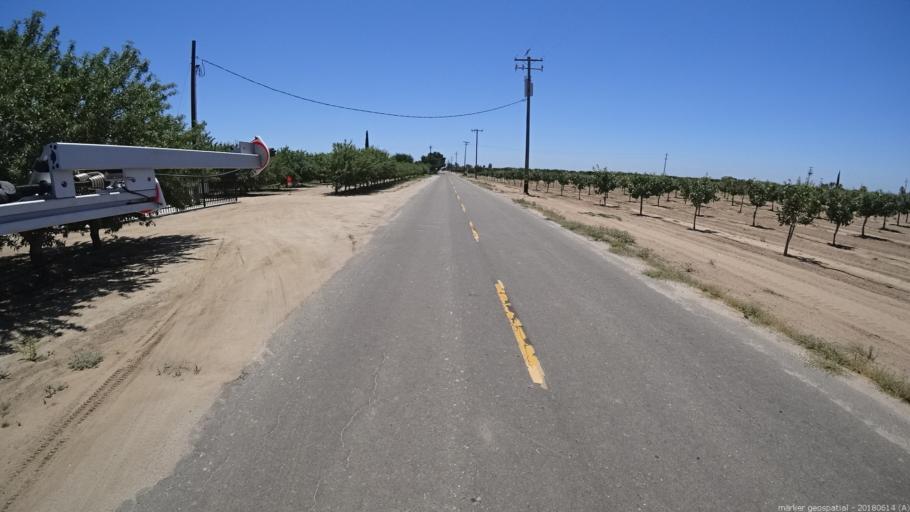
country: US
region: California
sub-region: Madera County
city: Fairmead
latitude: 37.0268
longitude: -120.1470
